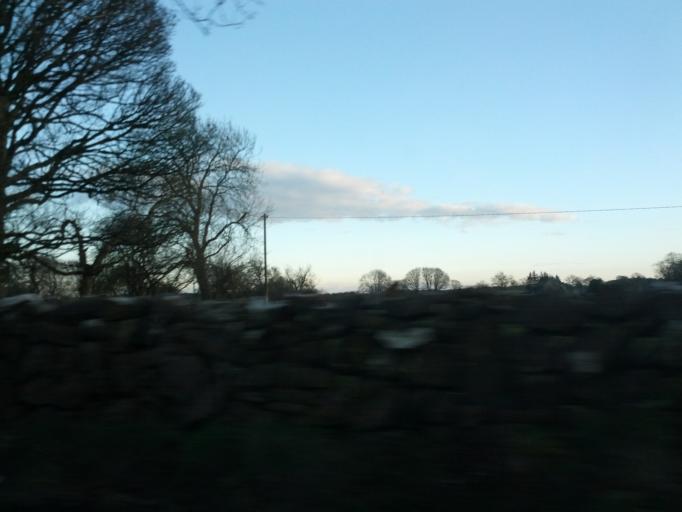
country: IE
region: Connaught
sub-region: County Galway
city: Athenry
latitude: 53.3241
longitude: -8.6729
